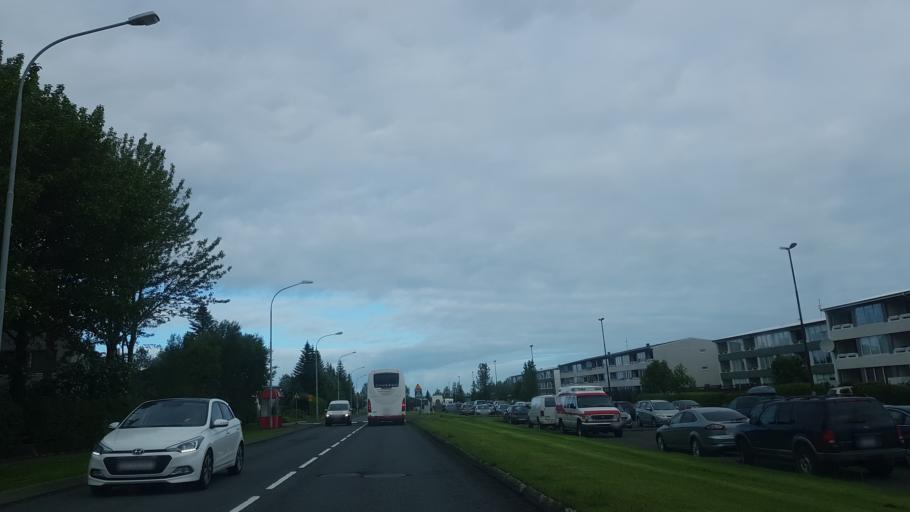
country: IS
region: Capital Region
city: Reykjavik
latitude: 64.0984
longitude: -21.8508
